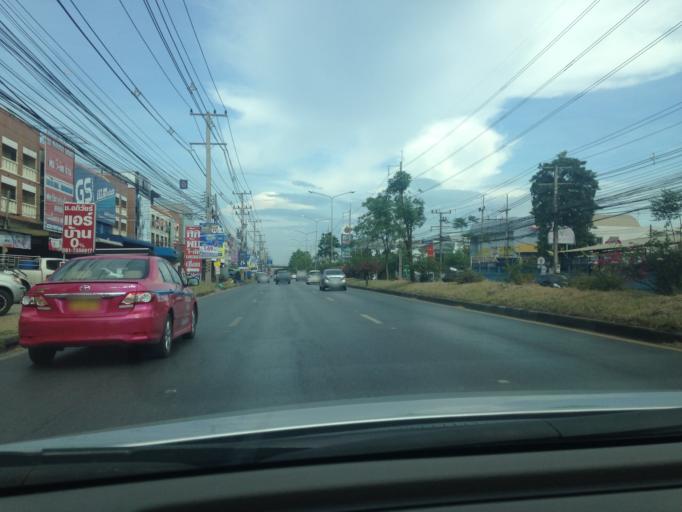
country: TH
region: Pathum Thani
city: Khlong Luang
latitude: 14.0659
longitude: 100.6593
